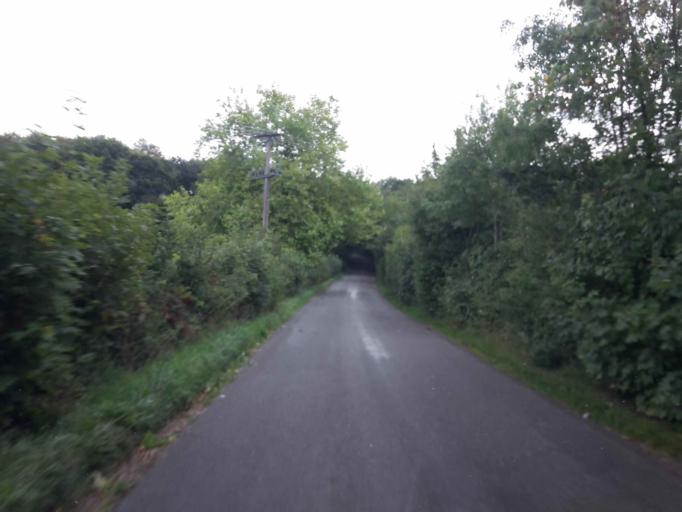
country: GB
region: England
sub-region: West Sussex
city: Billingshurst
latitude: 51.0306
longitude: -0.4370
